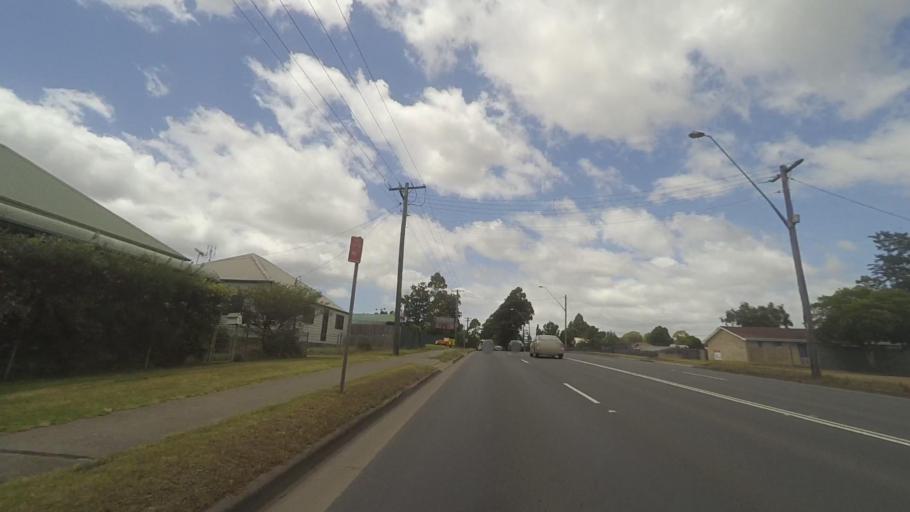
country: AU
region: New South Wales
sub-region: Shoalhaven Shire
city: Nowra
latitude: -34.8835
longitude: 150.6038
